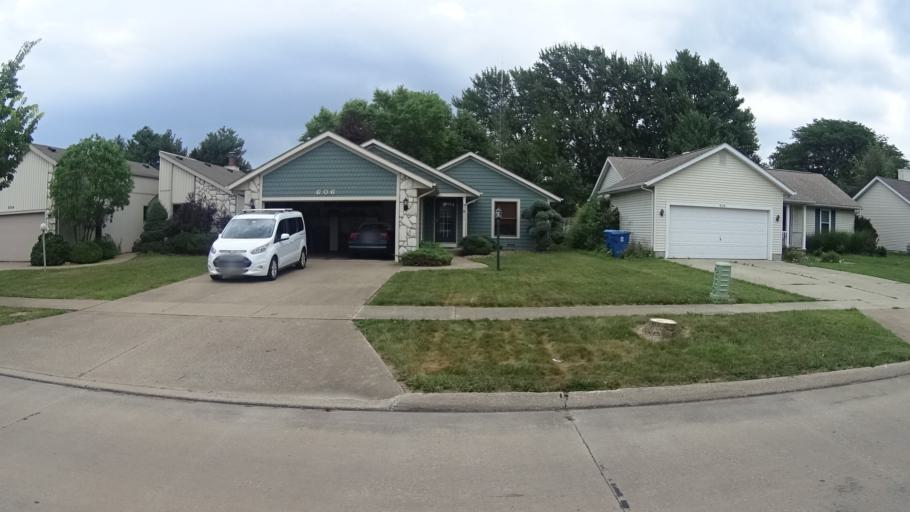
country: US
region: Ohio
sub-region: Erie County
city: Sandusky
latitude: 41.4400
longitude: -82.7655
